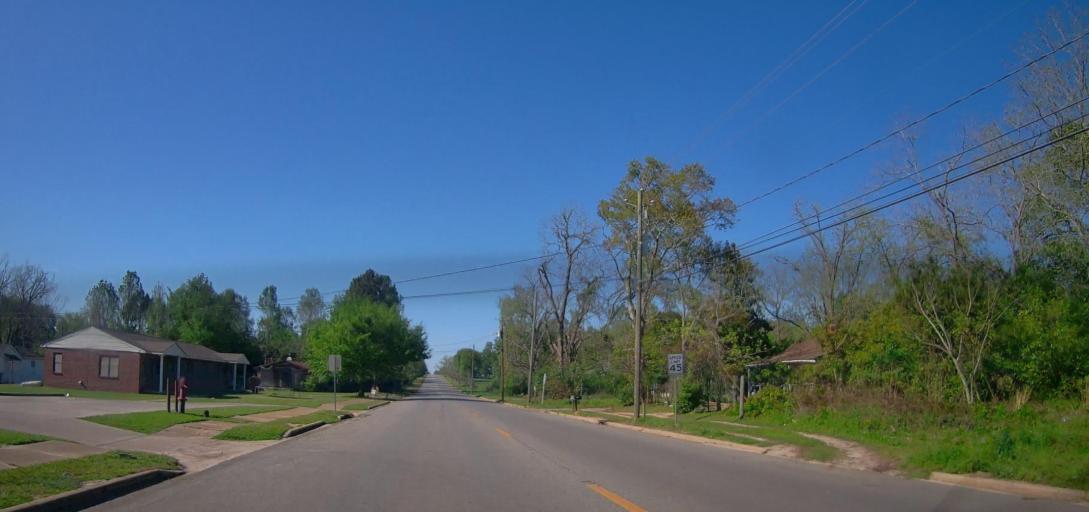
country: US
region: Georgia
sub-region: Wilcox County
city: Rochelle
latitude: 31.9537
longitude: -83.4563
